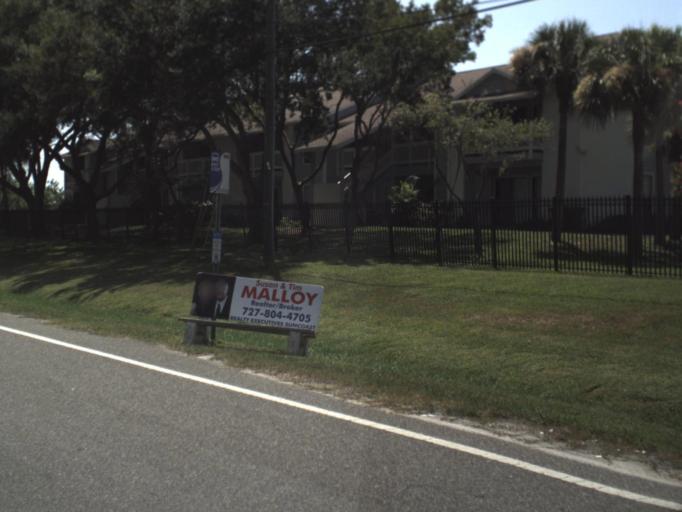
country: US
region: Florida
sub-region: Pinellas County
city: Palm Harbor
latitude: 28.0622
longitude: -82.7722
